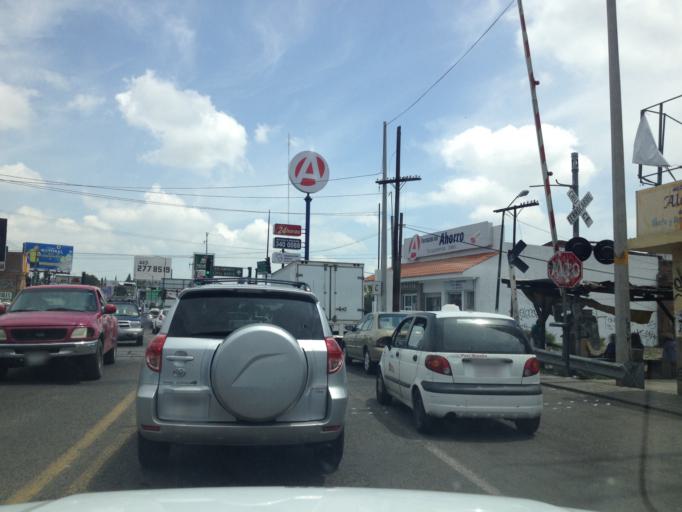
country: MX
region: Michoacan
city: Morelia
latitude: 19.7121
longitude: -101.1881
